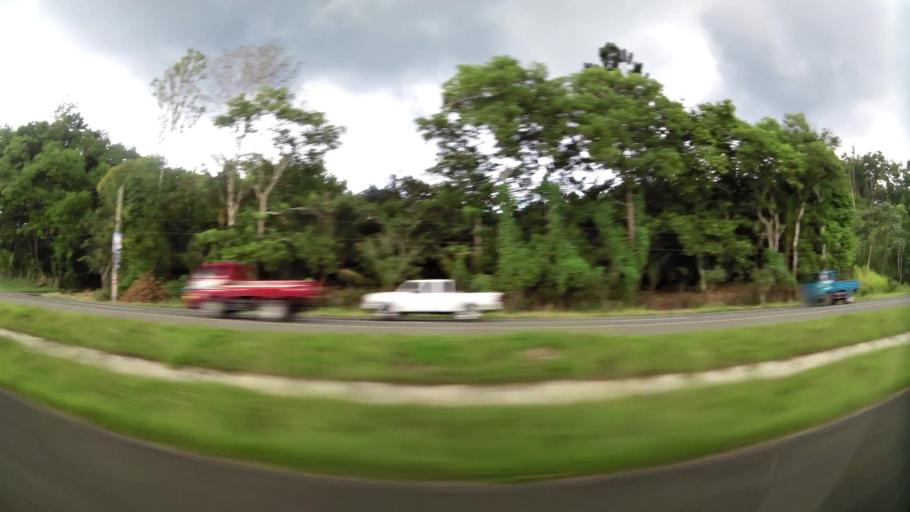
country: DO
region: San Cristobal
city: Villa Altagracia
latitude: 18.7442
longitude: -70.2320
